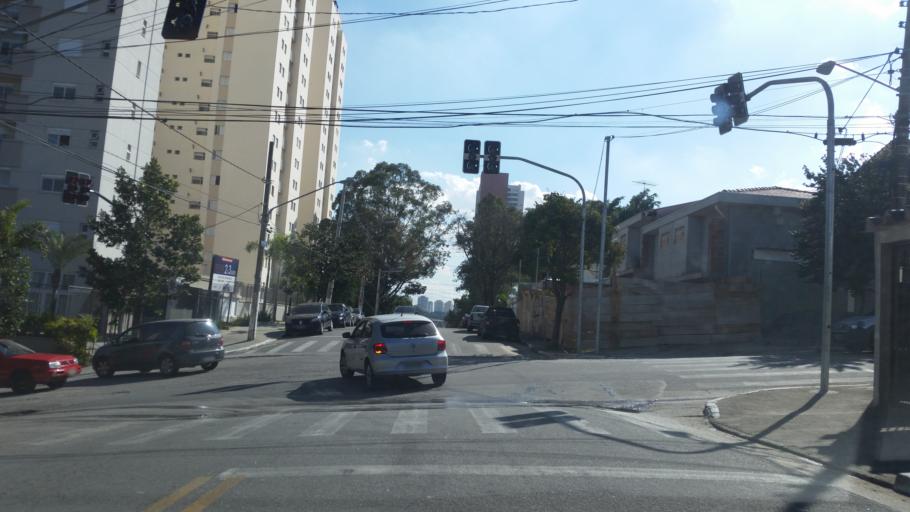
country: BR
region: Sao Paulo
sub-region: Diadema
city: Diadema
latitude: -23.6358
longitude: -46.6635
